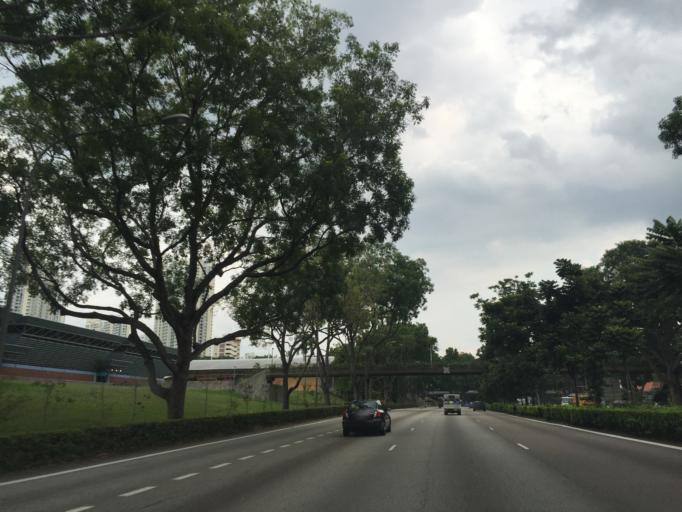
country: SG
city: Singapore
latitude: 1.3109
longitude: 103.7639
